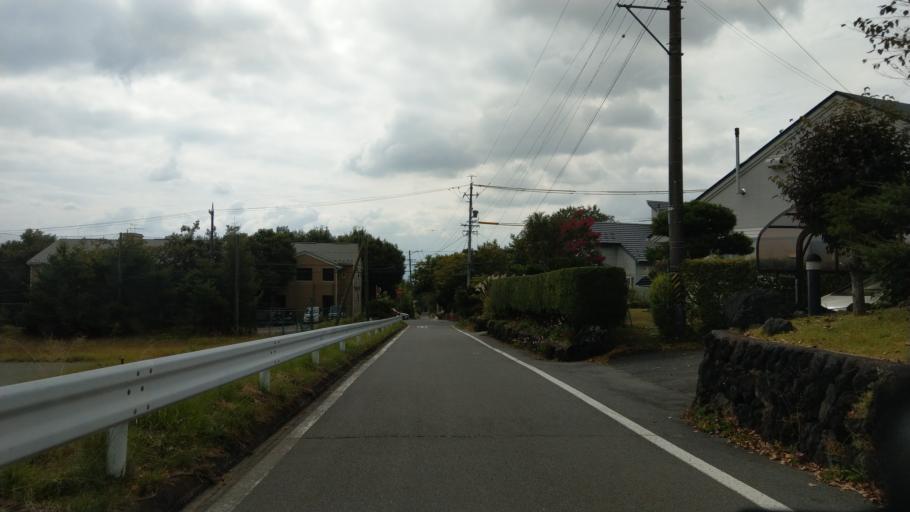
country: JP
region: Nagano
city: Komoro
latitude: 36.3228
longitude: 138.5260
